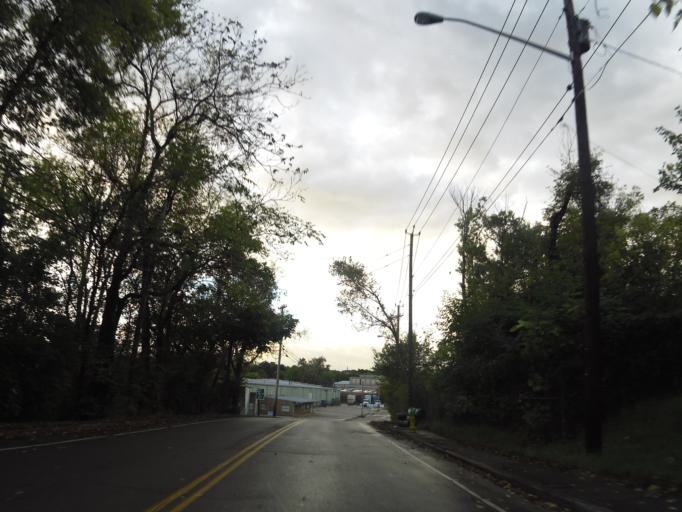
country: US
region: Tennessee
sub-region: Knox County
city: Knoxville
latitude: 35.9862
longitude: -83.9126
